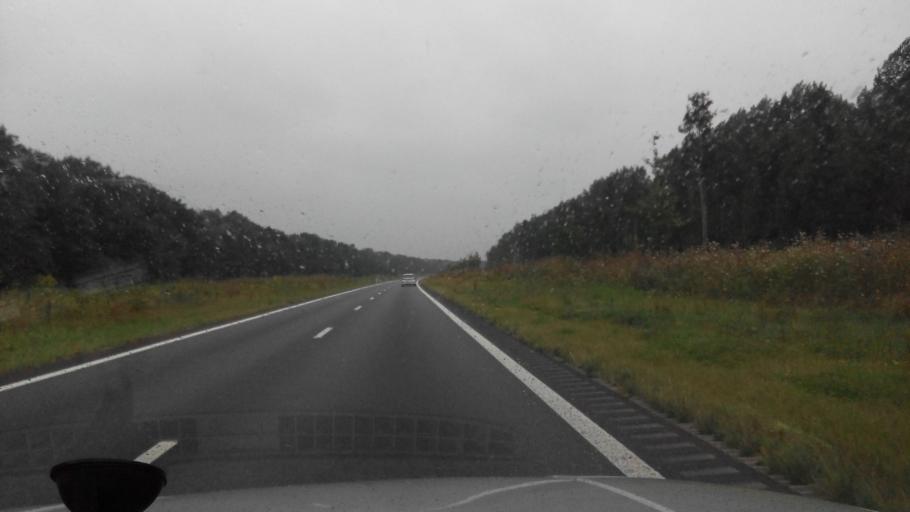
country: NL
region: Flevoland
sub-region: Gemeente Zeewolde
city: Zeewolde
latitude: 52.3381
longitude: 5.4851
